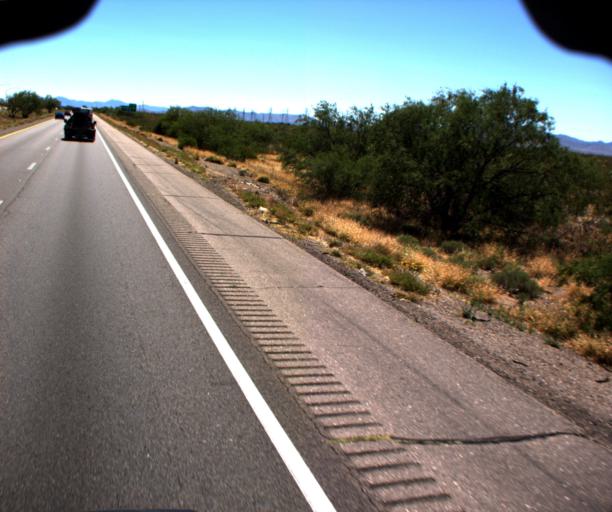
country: US
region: Arizona
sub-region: Pima County
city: Vail
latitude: 32.0668
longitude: -110.7823
